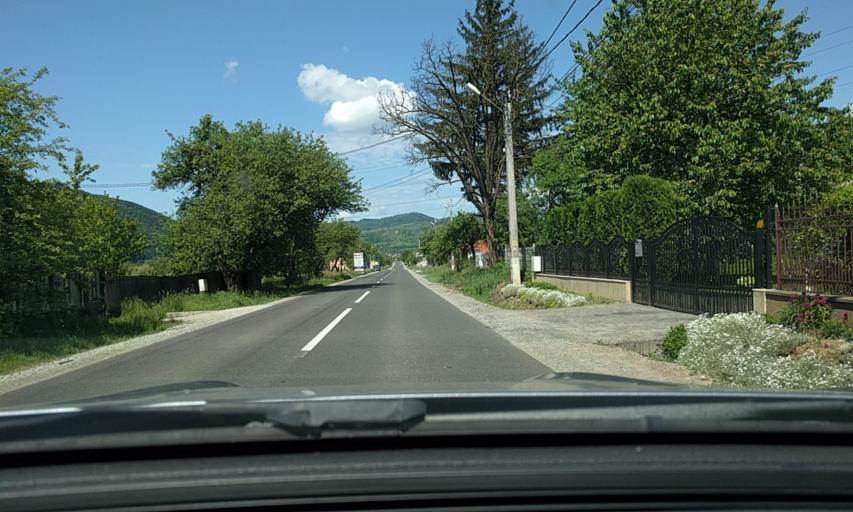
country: RO
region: Bistrita-Nasaud
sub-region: Oras Nasaud
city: Nasaud
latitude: 47.2973
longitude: 24.3786
